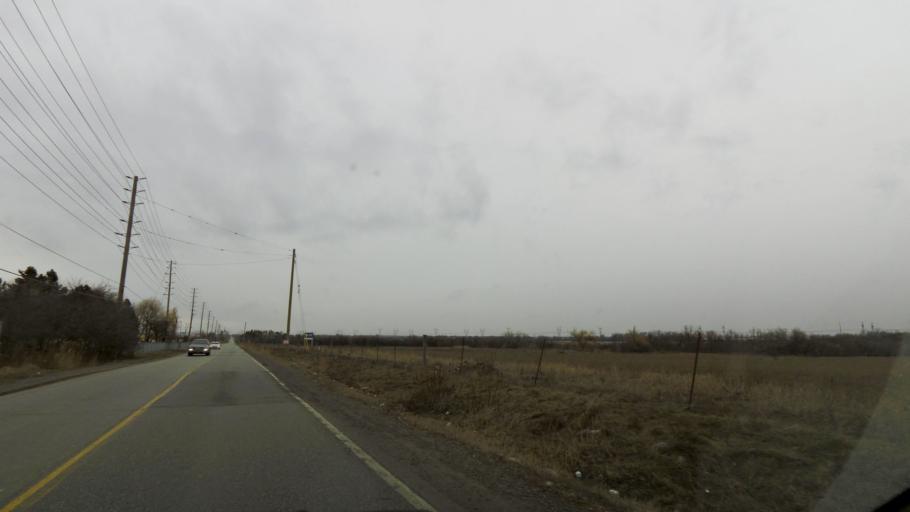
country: CA
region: Ontario
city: Brampton
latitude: 43.7903
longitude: -79.6519
